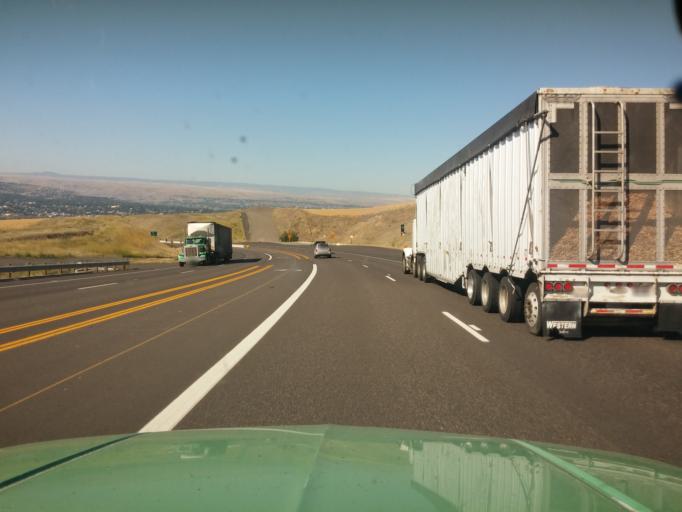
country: US
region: Idaho
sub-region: Nez Perce County
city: Lewiston
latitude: 46.4447
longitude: -116.9818
